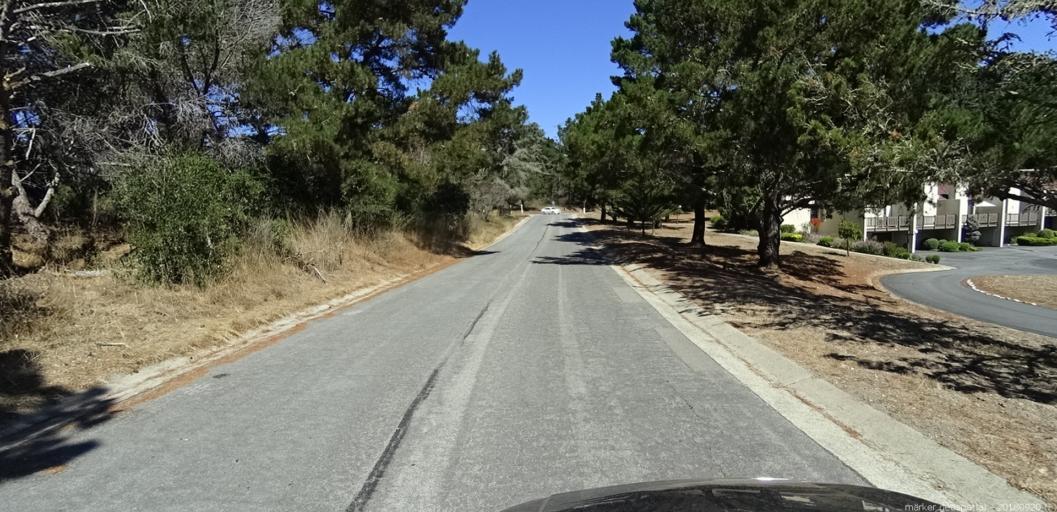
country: US
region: California
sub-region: Monterey County
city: Carmel-by-the-Sea
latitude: 36.5670
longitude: -121.9109
